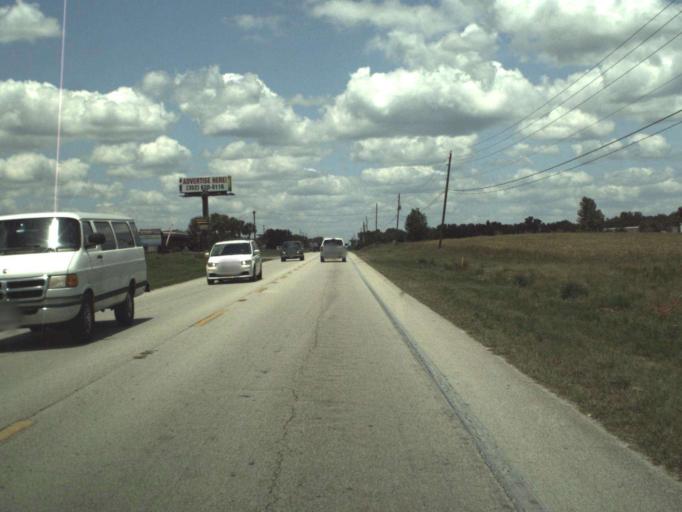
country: US
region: Florida
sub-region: Marion County
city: Silver Springs Shores
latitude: 29.1140
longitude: -82.0536
